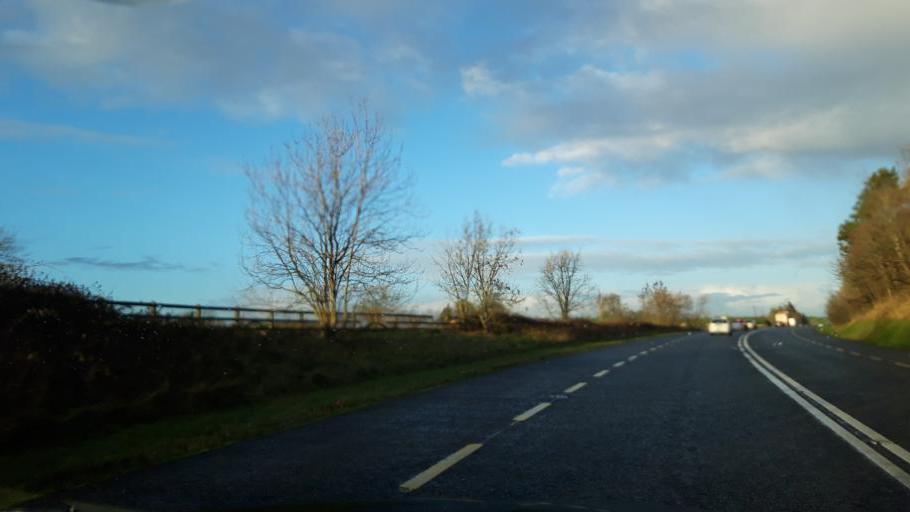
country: IE
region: Ulster
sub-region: County Monaghan
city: Carrickmacross
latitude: 54.0359
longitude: -6.7063
